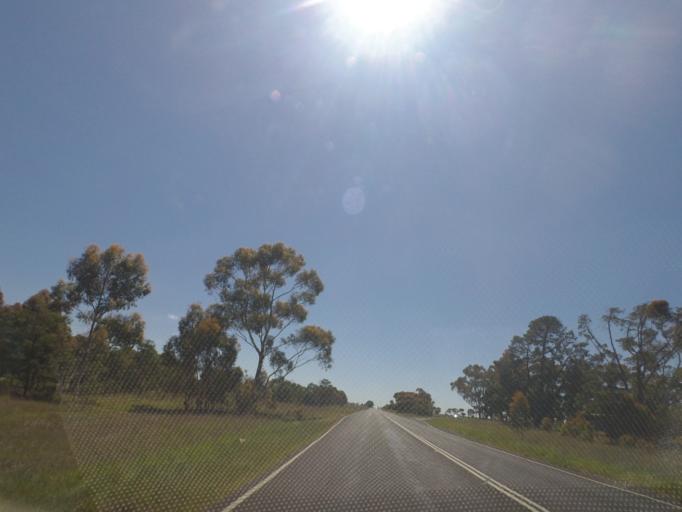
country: AU
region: Victoria
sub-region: Hume
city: Sunbury
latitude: -37.4914
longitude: 144.7567
